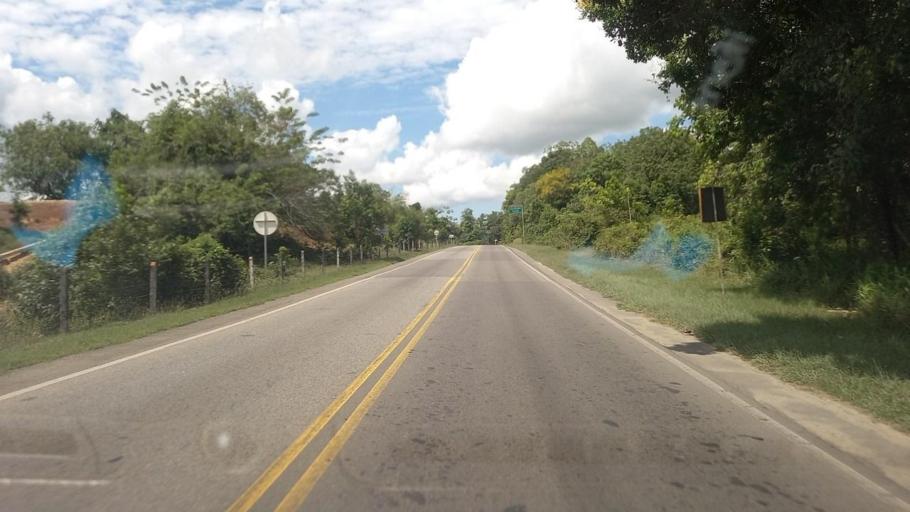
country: CO
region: Santander
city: Barrancabermeja
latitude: 7.1205
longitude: -73.5975
